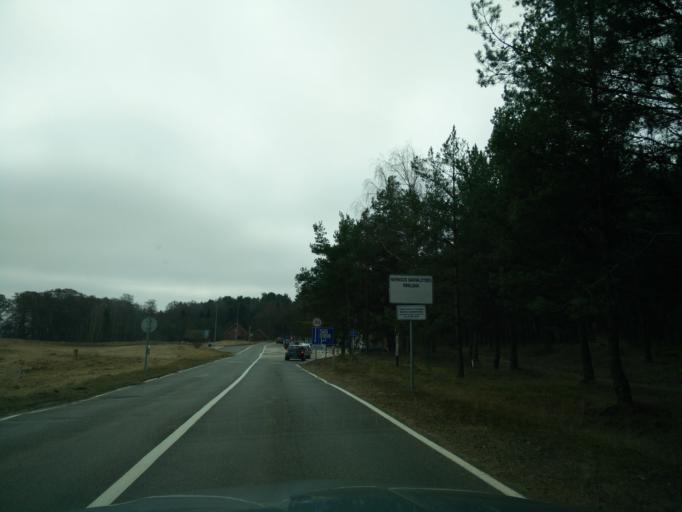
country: LT
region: Klaipedos apskritis
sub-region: Klaipeda
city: Klaipeda
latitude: 55.6344
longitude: 21.1299
